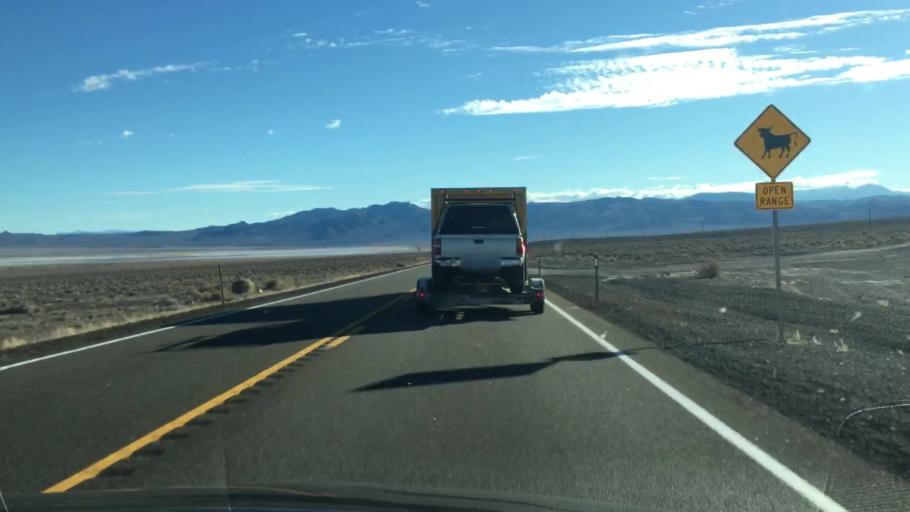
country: US
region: Nevada
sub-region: Mineral County
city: Hawthorne
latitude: 38.3376
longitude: -118.1031
